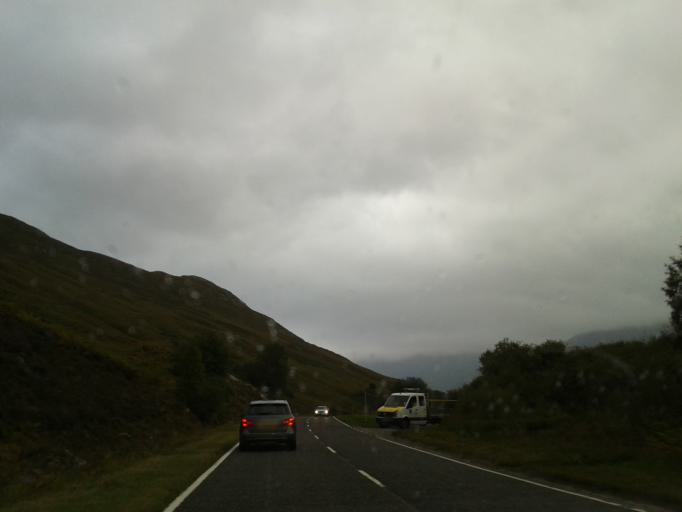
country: GB
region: Scotland
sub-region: Highland
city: Spean Bridge
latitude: 57.1533
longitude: -5.1296
